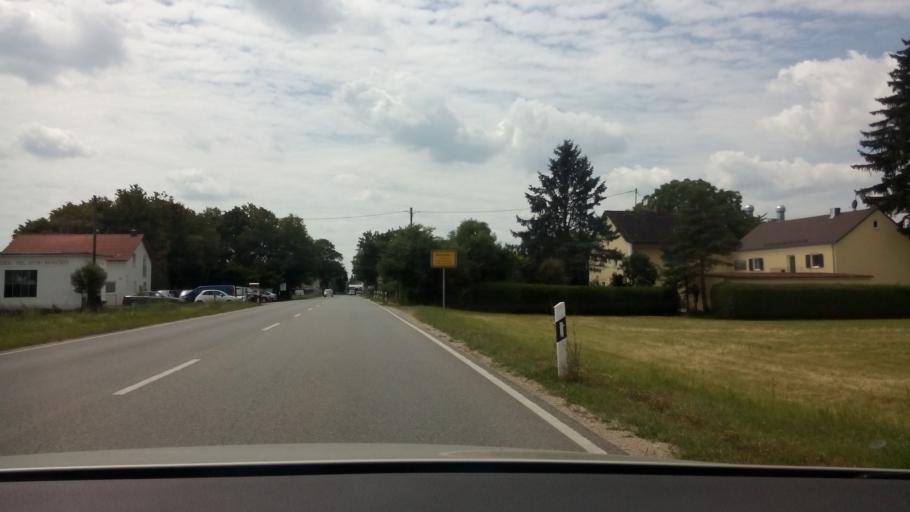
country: DE
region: Bavaria
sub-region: Upper Bavaria
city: Neufahrn bei Freising
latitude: 48.3216
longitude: 11.6922
